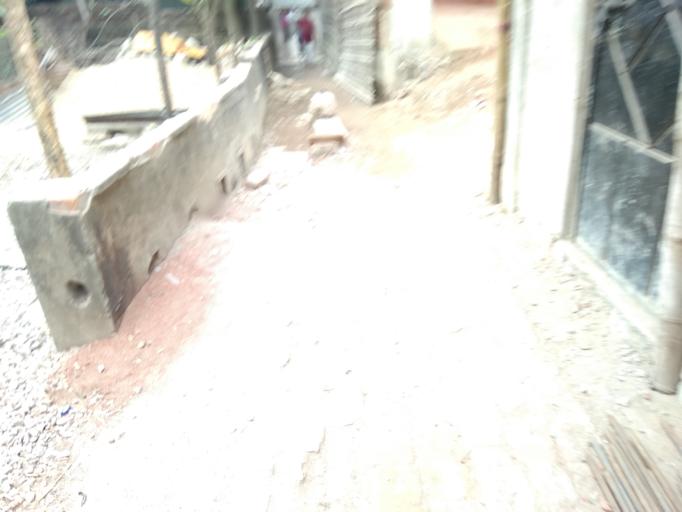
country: BD
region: Chittagong
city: Chittagong
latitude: 22.3708
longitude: 91.8365
